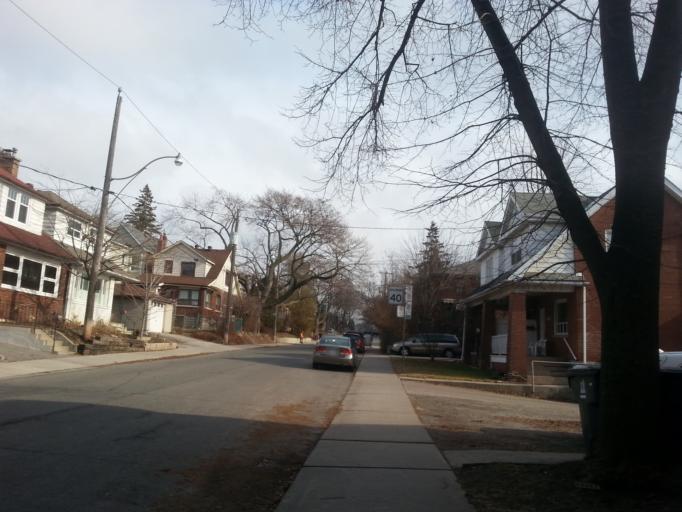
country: CA
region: Ontario
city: Toronto
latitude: 43.6784
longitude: -79.4327
